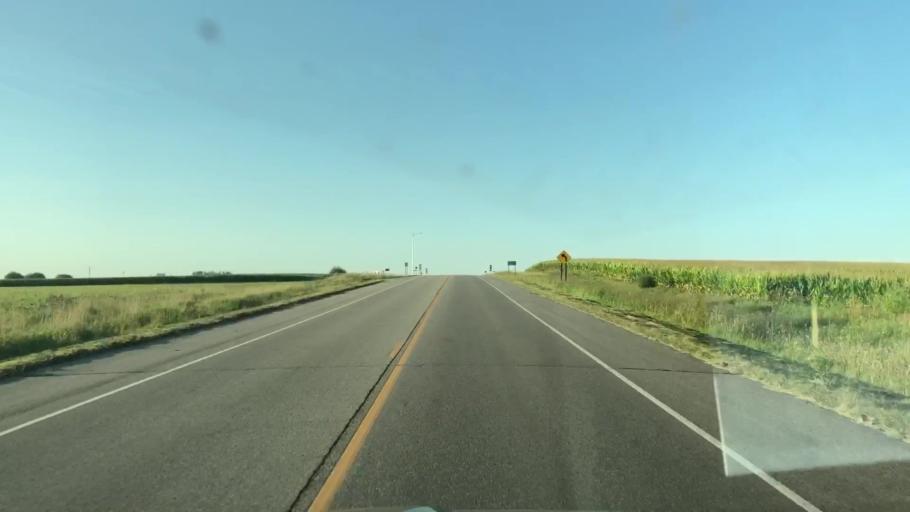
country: US
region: Minnesota
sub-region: Nobles County
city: Worthington
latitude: 43.6042
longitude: -95.6366
